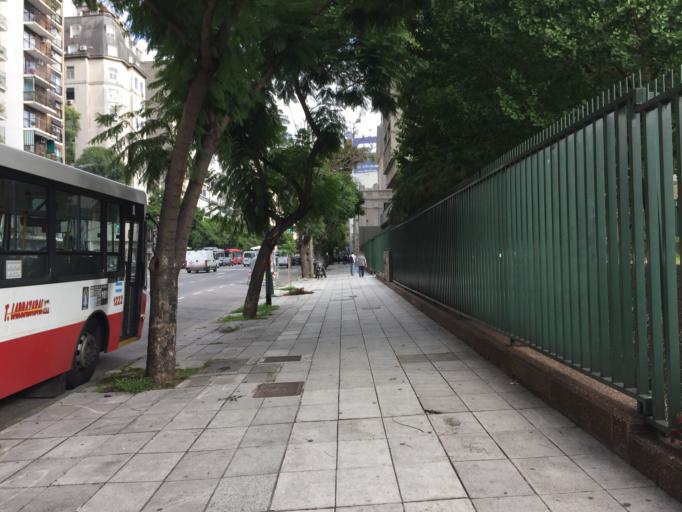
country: AR
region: Buenos Aires F.D.
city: Colegiales
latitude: -34.5724
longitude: -58.4400
